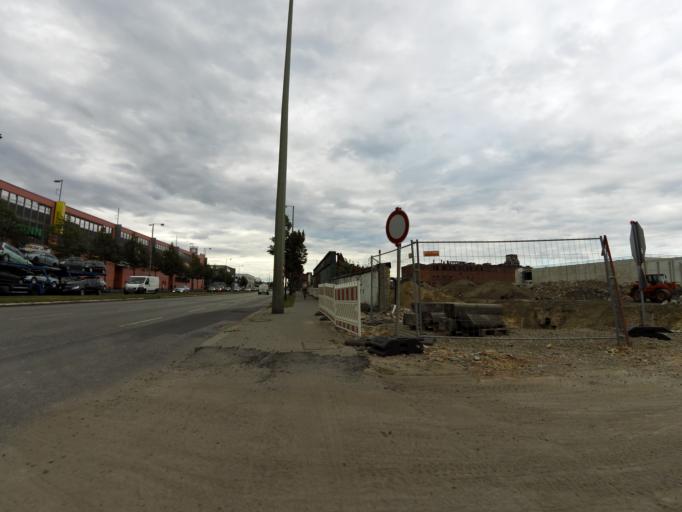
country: DE
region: Berlin
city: Niederschoneweide
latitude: 52.4574
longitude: 13.5088
